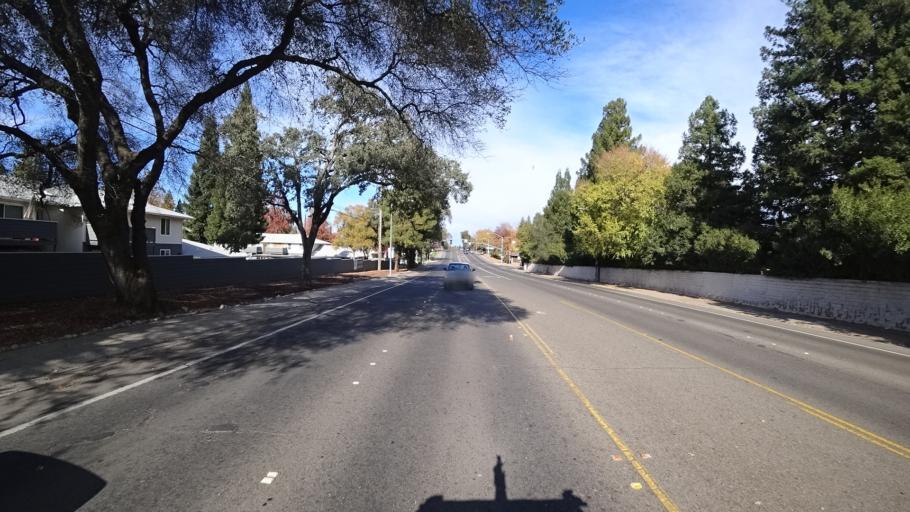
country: US
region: California
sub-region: Sacramento County
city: Fair Oaks
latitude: 38.6713
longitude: -121.2622
